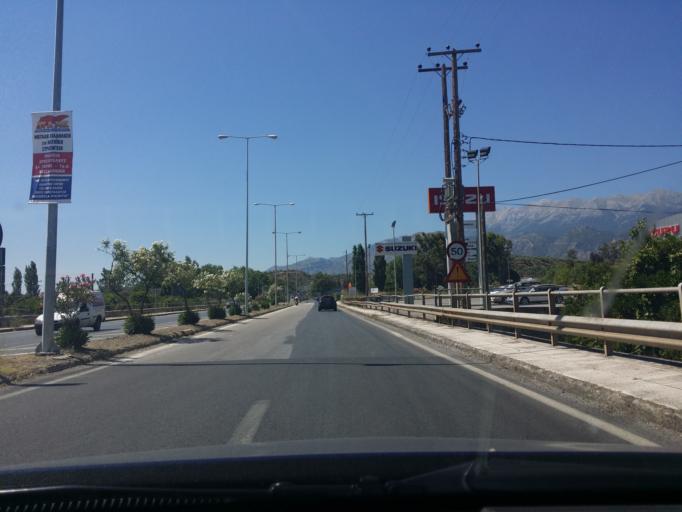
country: GR
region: Peloponnese
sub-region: Nomos Lakonias
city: Sparti
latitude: 37.0908
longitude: 22.4311
